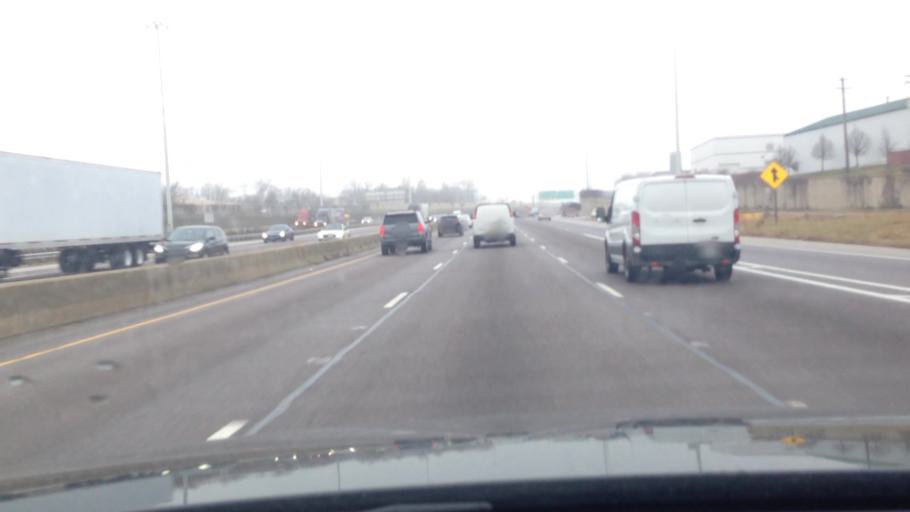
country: US
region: Illinois
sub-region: Cook County
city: Bellwood
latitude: 41.8698
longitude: -87.8844
